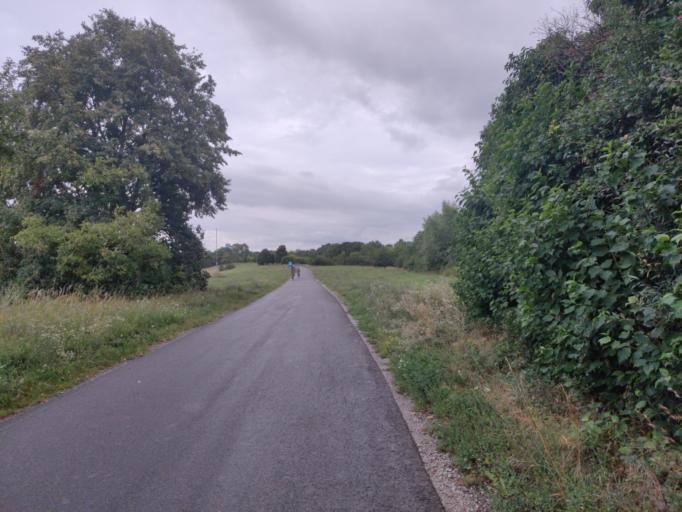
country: AT
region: Lower Austria
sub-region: Politischer Bezirk Korneuburg
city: Langenzersdorf
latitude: 48.2767
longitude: 16.3625
